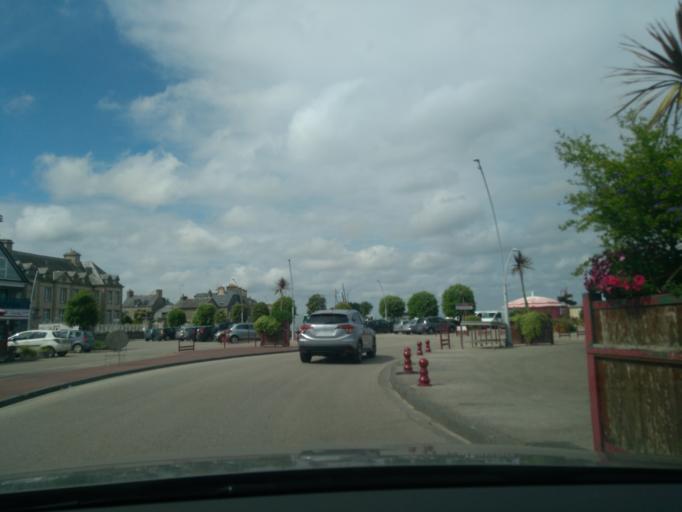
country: FR
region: Lower Normandy
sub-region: Departement de la Manche
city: Saint-Vaast-la-Hougue
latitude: 49.5894
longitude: -1.2663
